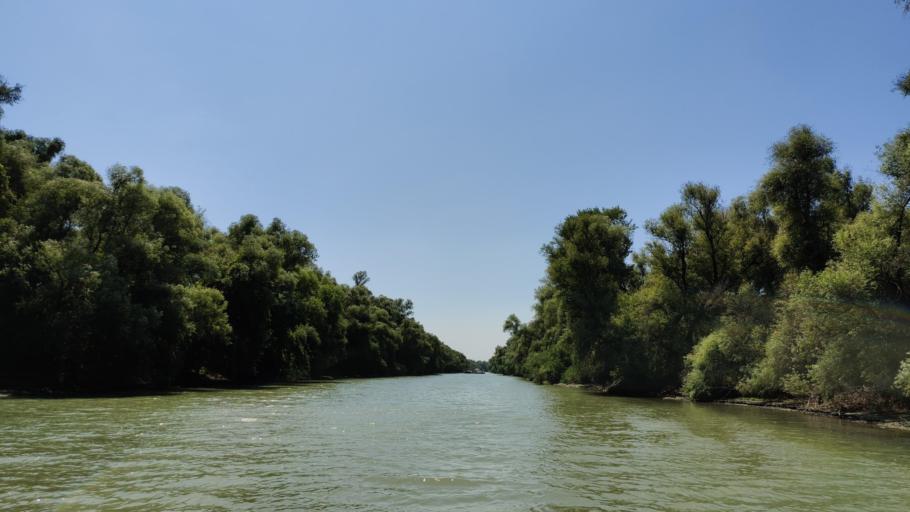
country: RO
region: Tulcea
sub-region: Comuna Pardina
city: Pardina
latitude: 45.2486
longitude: 28.9239
